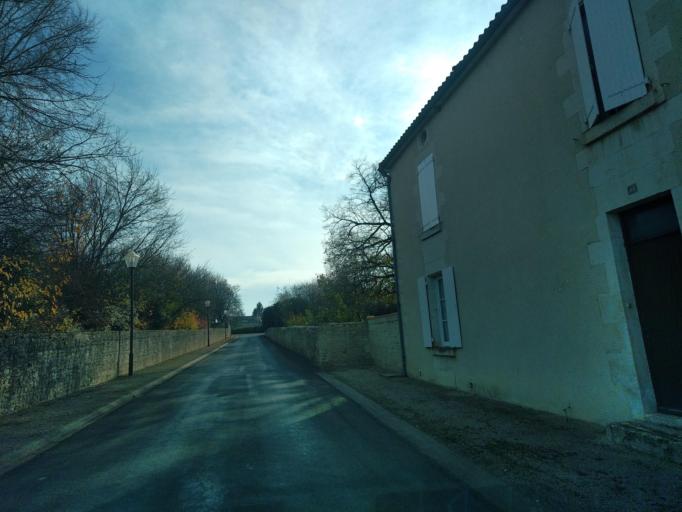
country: FR
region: Pays de la Loire
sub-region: Departement de la Vendee
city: Maillezais
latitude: 46.3700
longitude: -0.7422
